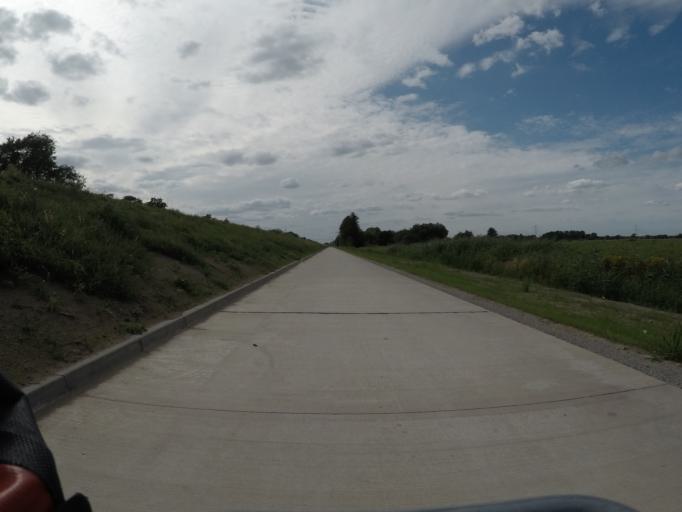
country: DE
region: Lower Saxony
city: Handorf
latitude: 53.3550
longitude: 10.3604
